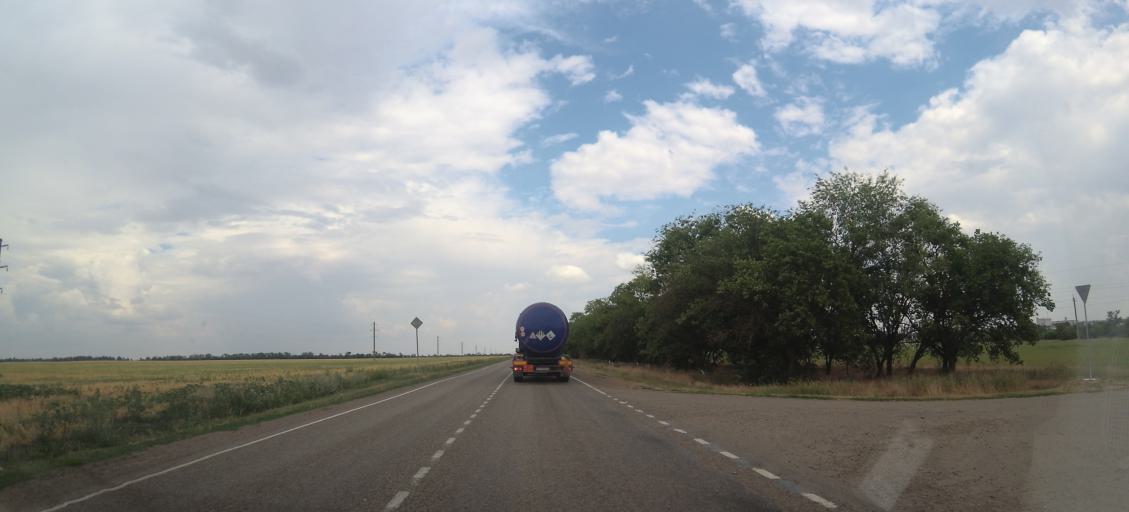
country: RU
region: Rostov
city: Peschanokopskoye
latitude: 46.2483
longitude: 41.2761
